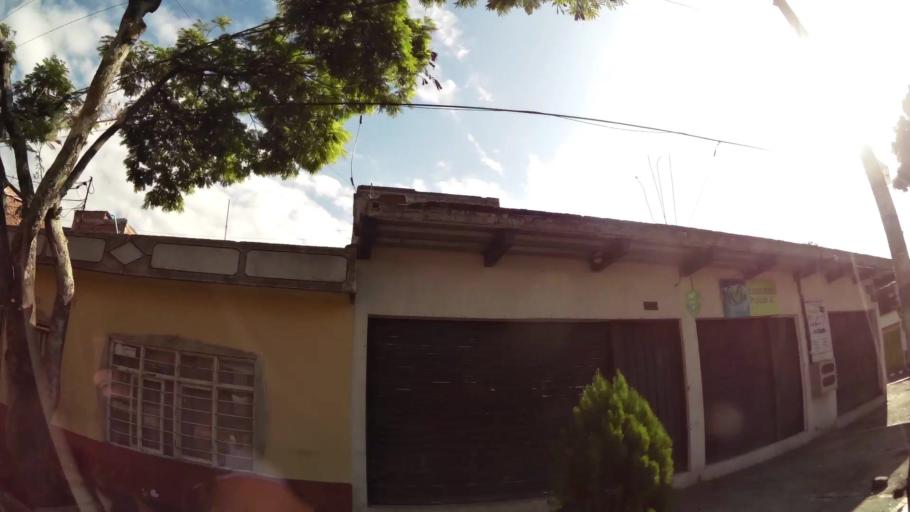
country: CO
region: Valle del Cauca
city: Cali
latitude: 3.4306
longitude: -76.5089
